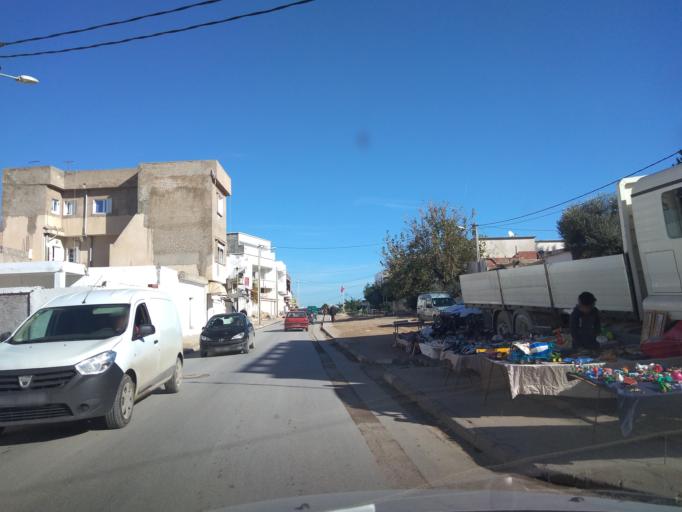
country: TN
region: Manouba
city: Manouba
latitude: 36.7993
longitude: 10.0902
